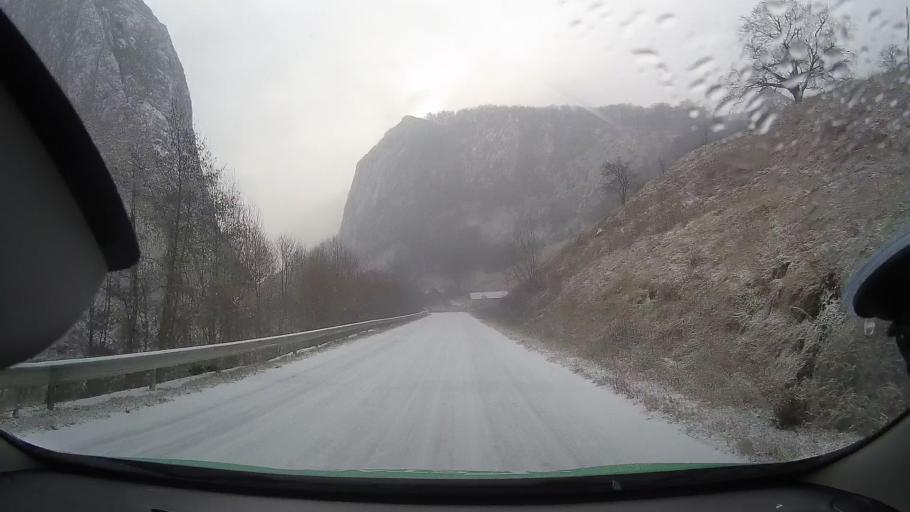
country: RO
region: Alba
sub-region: Comuna Livezile
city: Livezile
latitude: 46.3768
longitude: 23.5828
